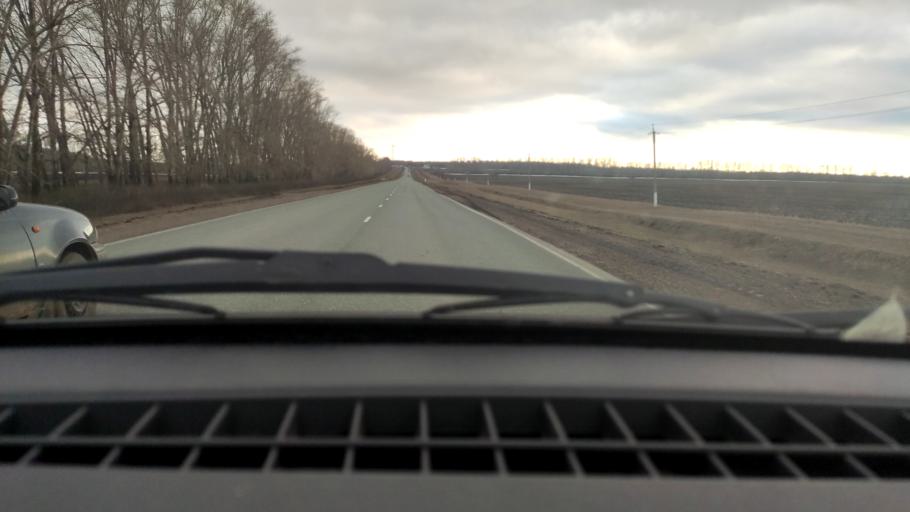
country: RU
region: Bashkortostan
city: Chishmy
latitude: 54.6498
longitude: 55.3855
